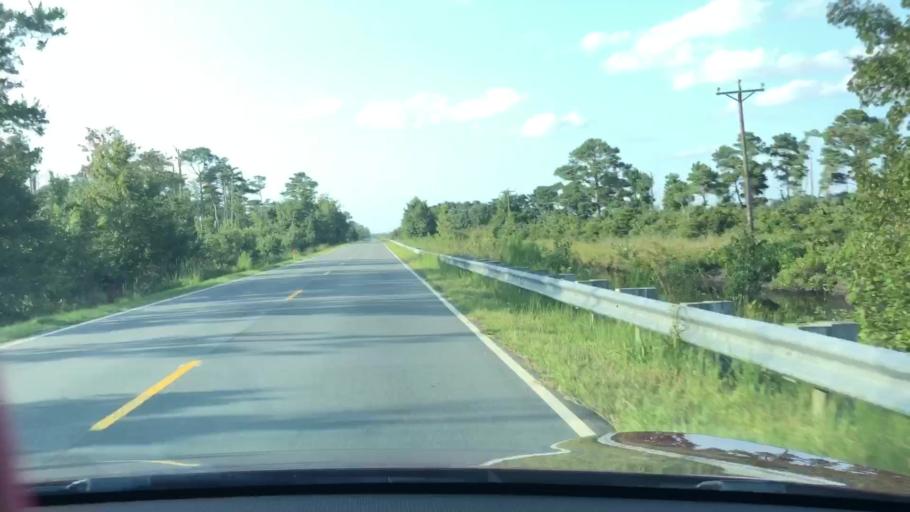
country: US
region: North Carolina
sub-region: Dare County
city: Wanchese
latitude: 35.6689
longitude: -75.7784
